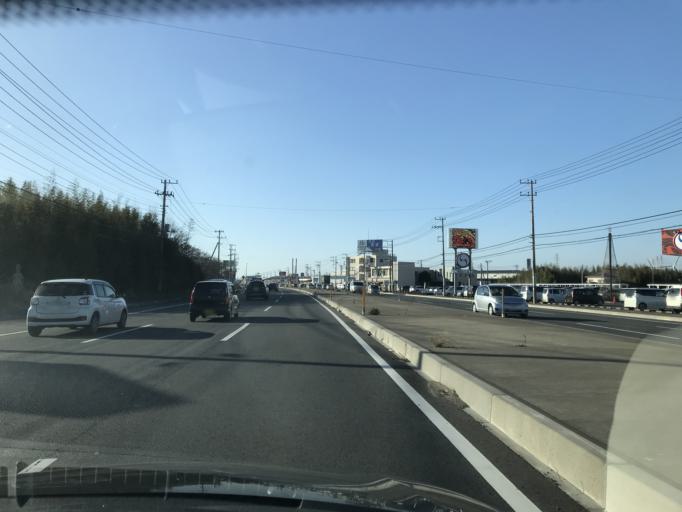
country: JP
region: Chiba
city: Omigawa
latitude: 35.8816
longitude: 140.6819
